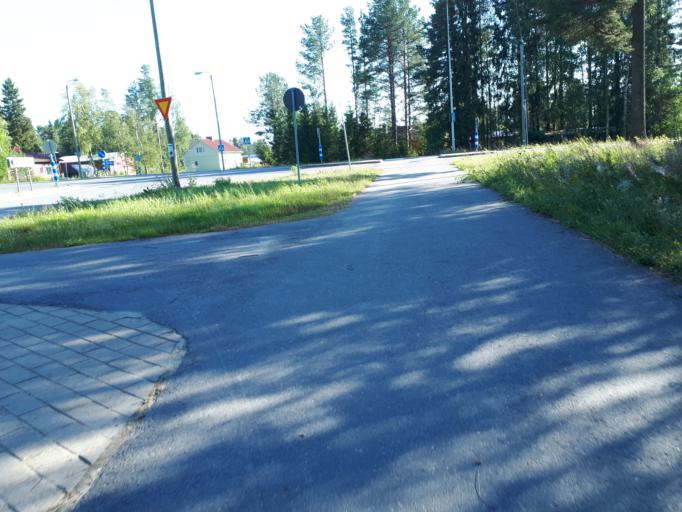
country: FI
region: Northern Ostrobothnia
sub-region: Oulunkaari
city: Ii
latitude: 65.3167
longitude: 25.3870
